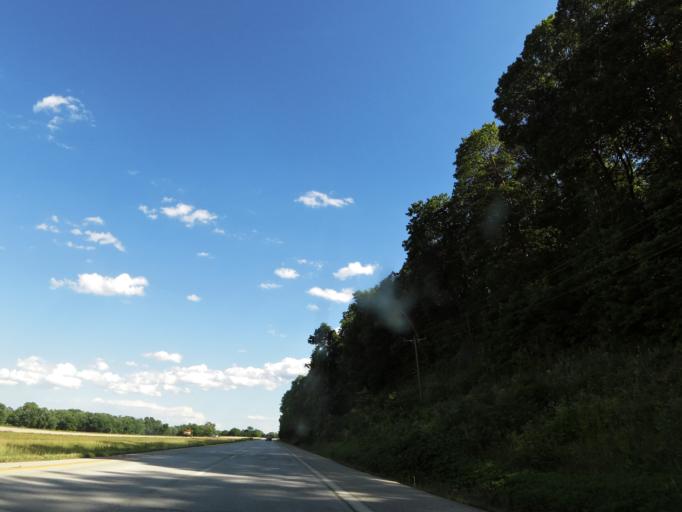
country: US
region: Missouri
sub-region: Lewis County
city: Canton
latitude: 40.2267
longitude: -91.5297
